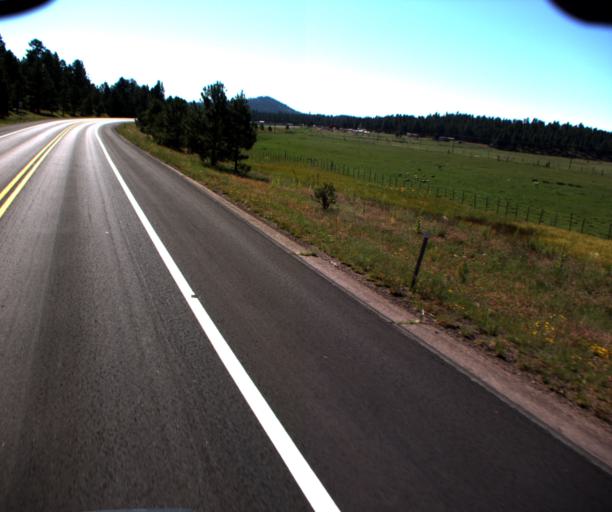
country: US
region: Arizona
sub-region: Apache County
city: Eagar
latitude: 33.8368
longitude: -109.1228
